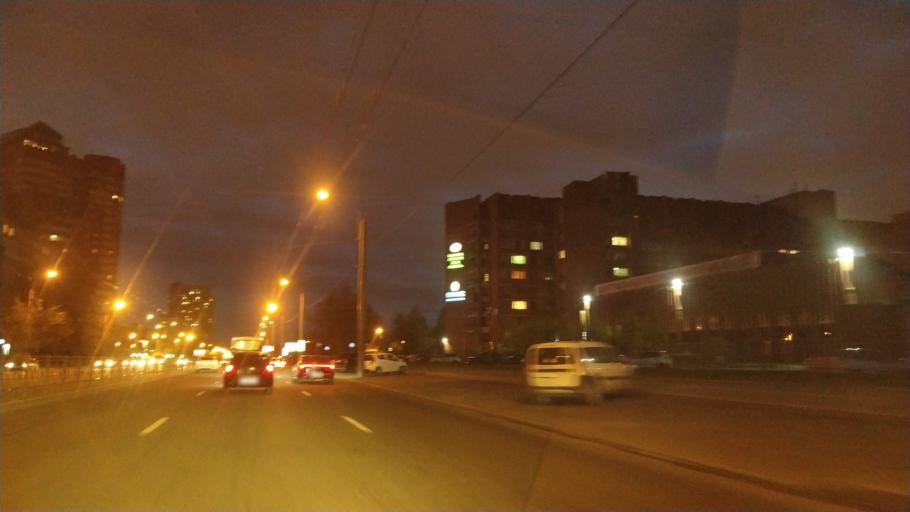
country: RU
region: St.-Petersburg
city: Sosnovka
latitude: 60.0373
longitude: 30.3603
